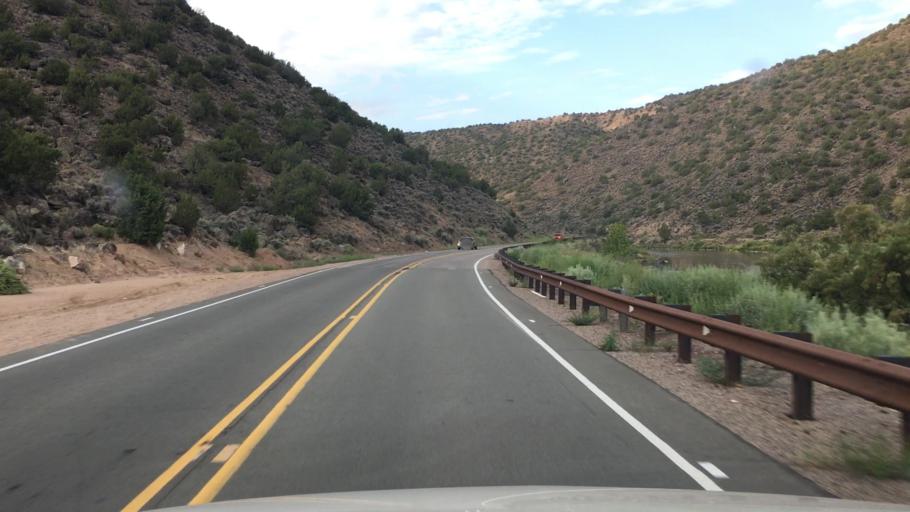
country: US
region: New Mexico
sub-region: Rio Arriba County
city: Ohkay Owingeh
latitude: 36.1892
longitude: -105.9790
